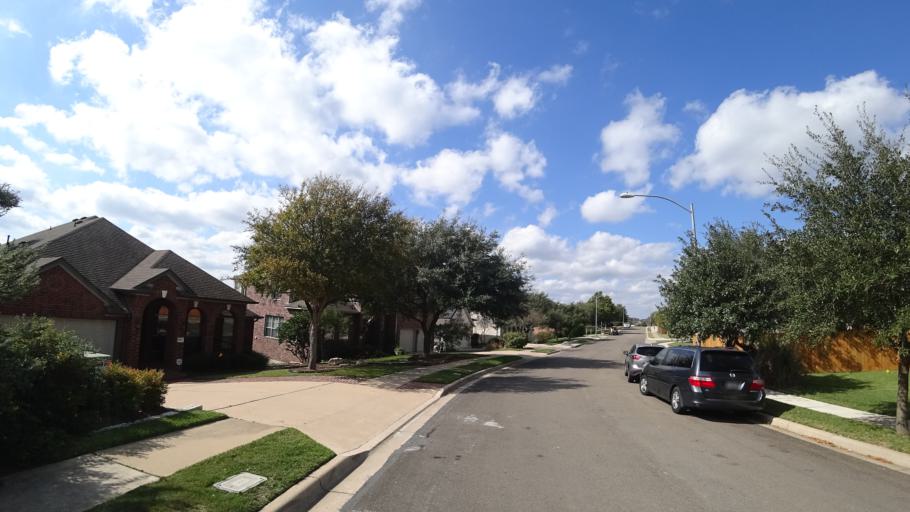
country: US
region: Texas
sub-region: Travis County
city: Barton Creek
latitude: 30.2534
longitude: -97.8846
